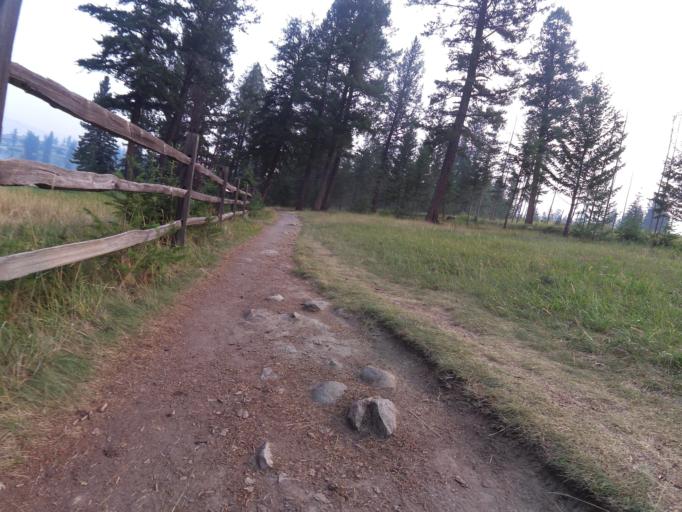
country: CA
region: Alberta
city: Jasper Park Lodge
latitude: 52.8799
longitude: -118.0552
